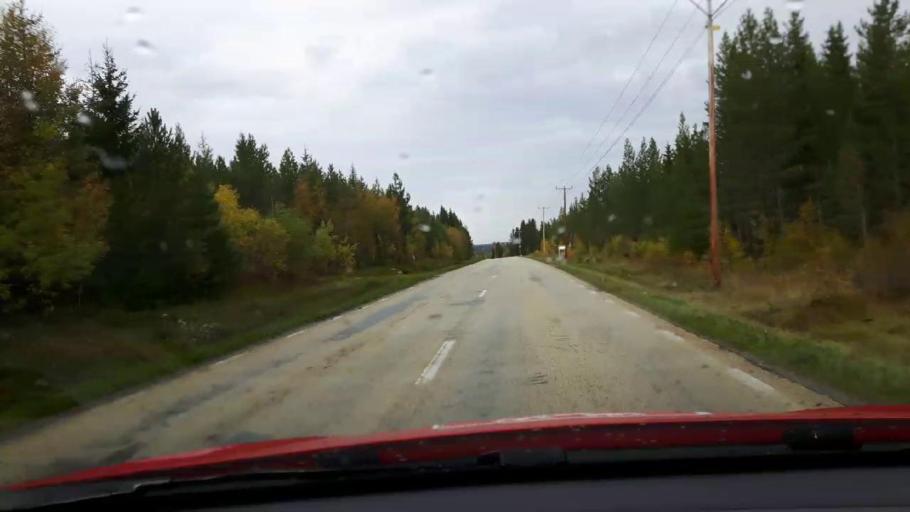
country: SE
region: Jaemtland
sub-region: Bergs Kommun
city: Hoverberg
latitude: 62.9663
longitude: 14.3486
